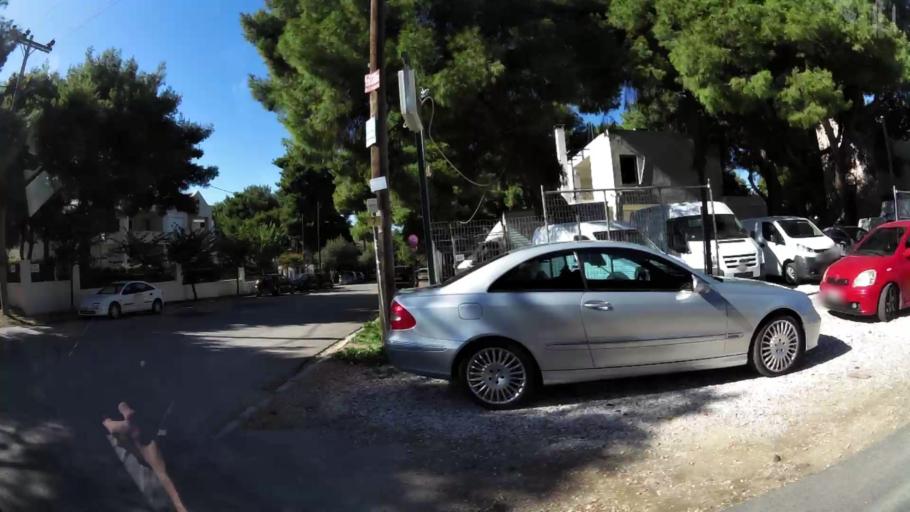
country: GR
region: Attica
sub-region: Nomarchia Athinas
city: Nea Erythraia
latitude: 38.1004
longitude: 23.8121
